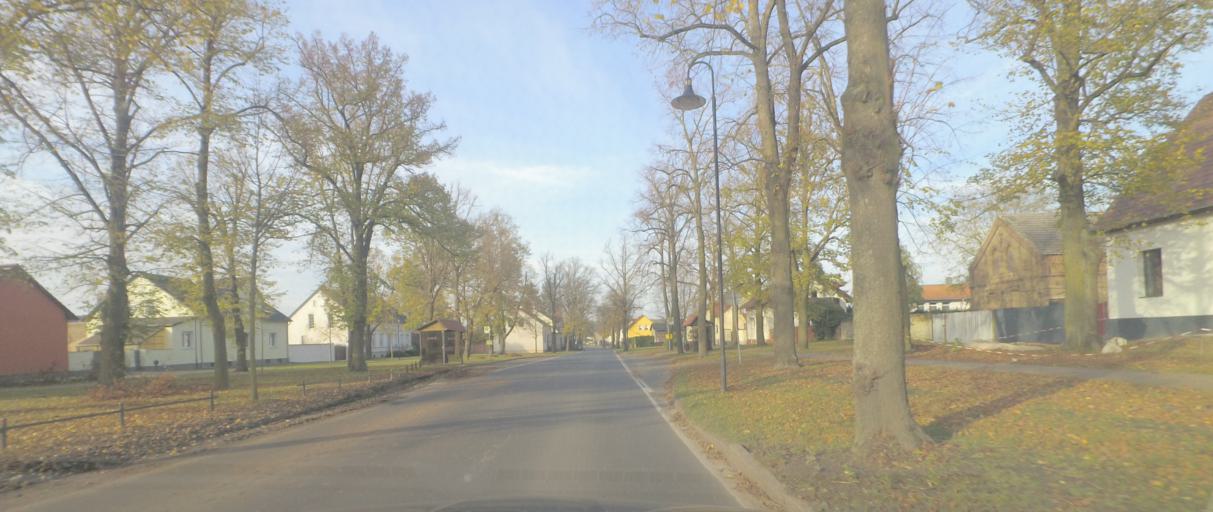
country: DE
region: Brandenburg
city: Rangsdorf
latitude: 52.2522
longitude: 13.3795
